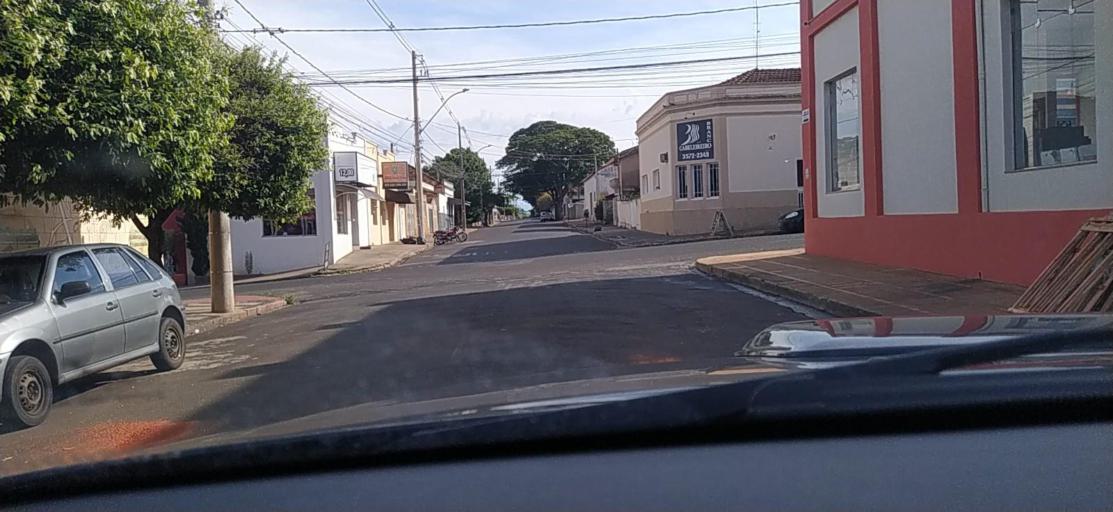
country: BR
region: Sao Paulo
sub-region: Pindorama
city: Pindorama
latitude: -21.1896
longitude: -48.9032
